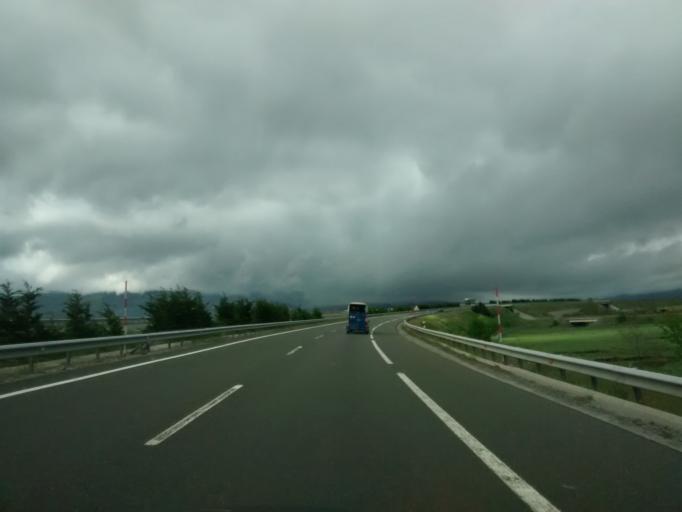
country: ES
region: Cantabria
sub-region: Provincia de Cantabria
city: Villaescusa
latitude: 42.9715
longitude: -4.1563
